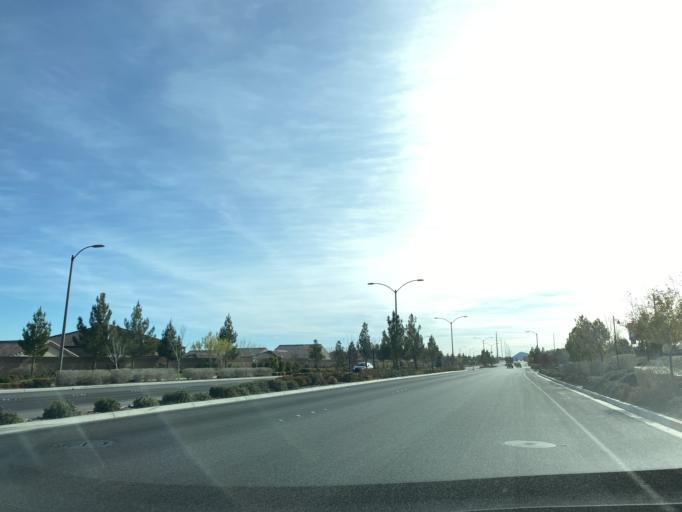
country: US
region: Nevada
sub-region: Clark County
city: Summerlin South
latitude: 36.3132
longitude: -115.3150
